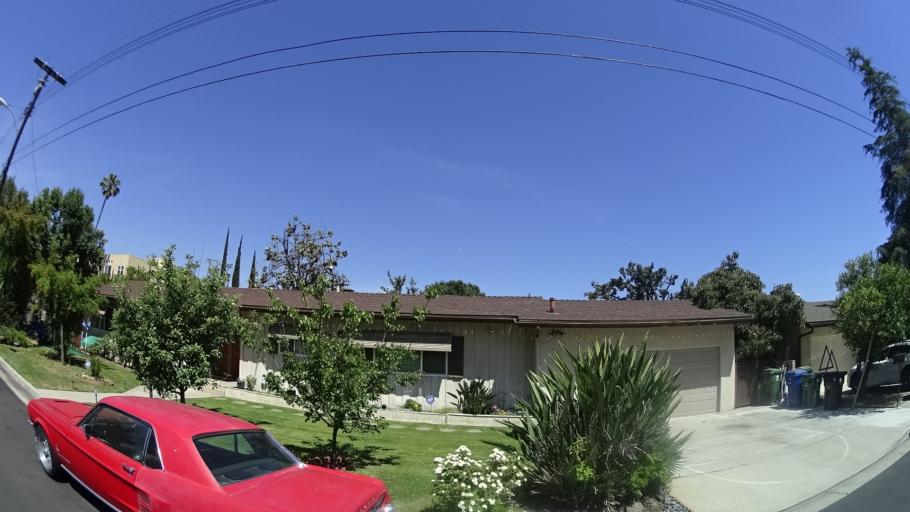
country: US
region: California
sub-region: Los Angeles County
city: North Hollywood
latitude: 34.1733
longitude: -118.3976
